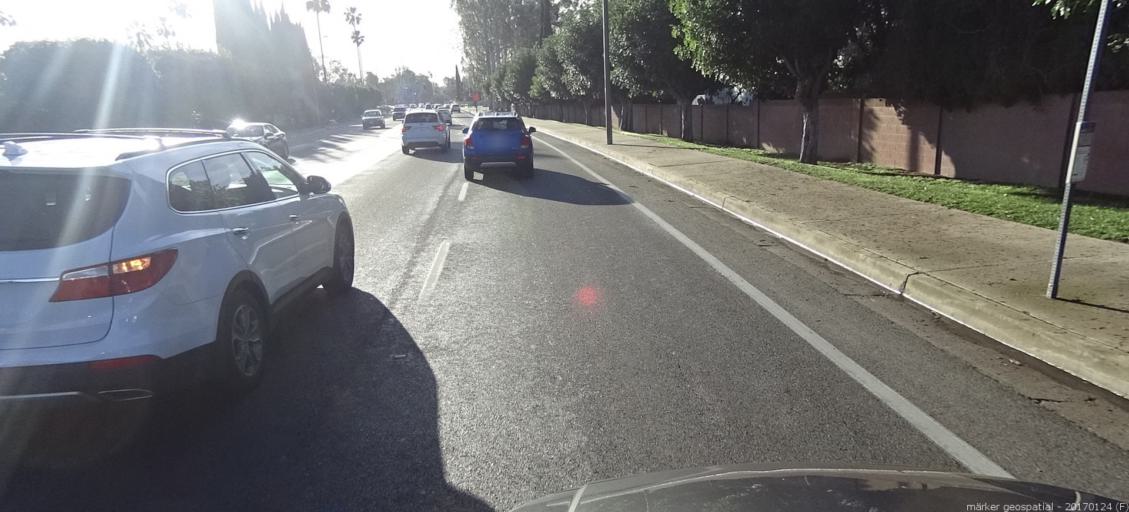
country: US
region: California
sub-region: Orange County
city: Laguna Hills
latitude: 33.6192
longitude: -117.6946
